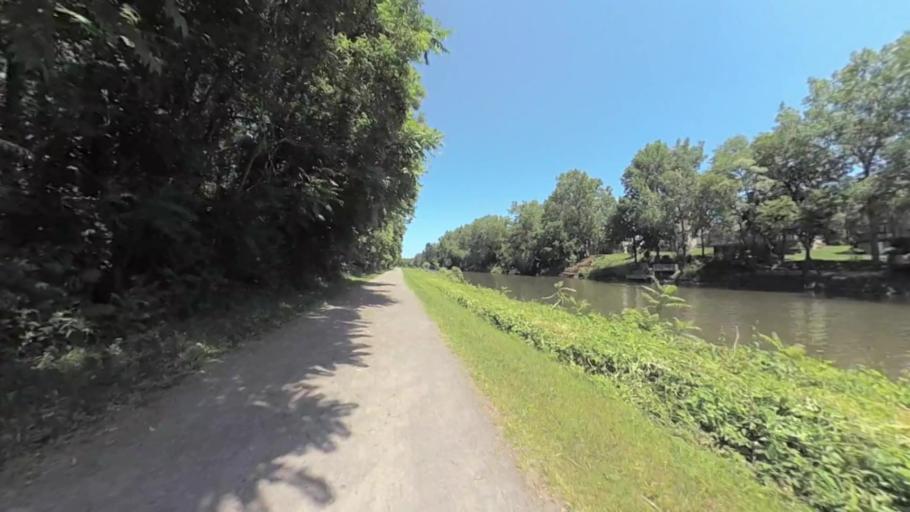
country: US
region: New York
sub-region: Monroe County
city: Fairport
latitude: 43.0913
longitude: -77.4559
